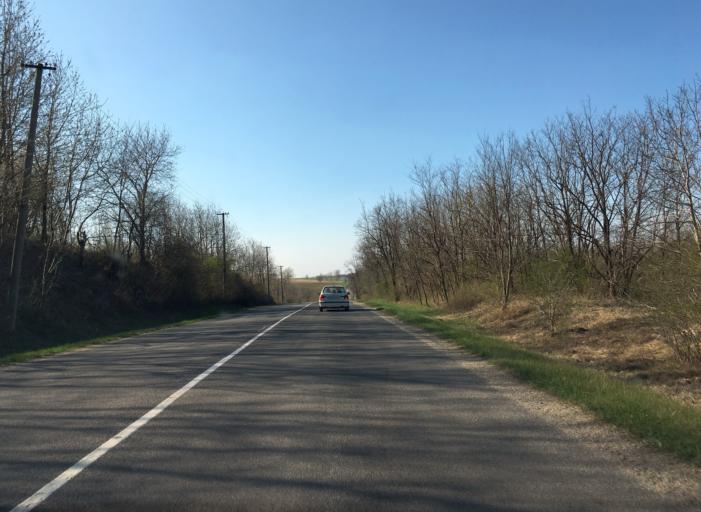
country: SK
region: Nitriansky
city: Svodin
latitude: 47.8718
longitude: 18.4546
